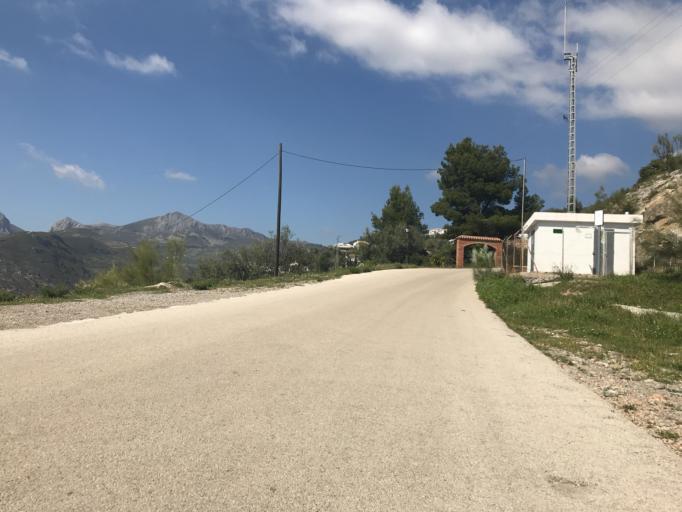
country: ES
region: Andalusia
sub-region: Provincia de Malaga
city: Alcaucin
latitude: 36.9056
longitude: -4.1123
